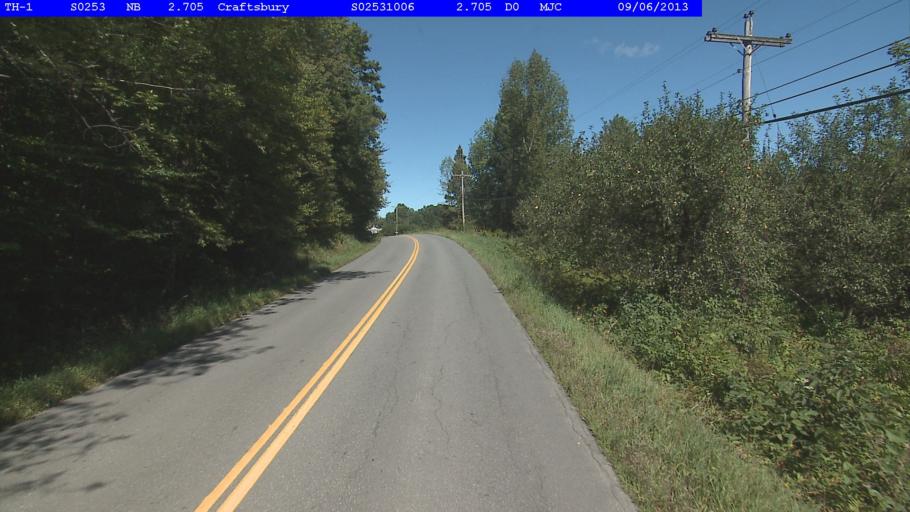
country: US
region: Vermont
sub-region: Caledonia County
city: Hardwick
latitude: 44.6473
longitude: -72.3800
